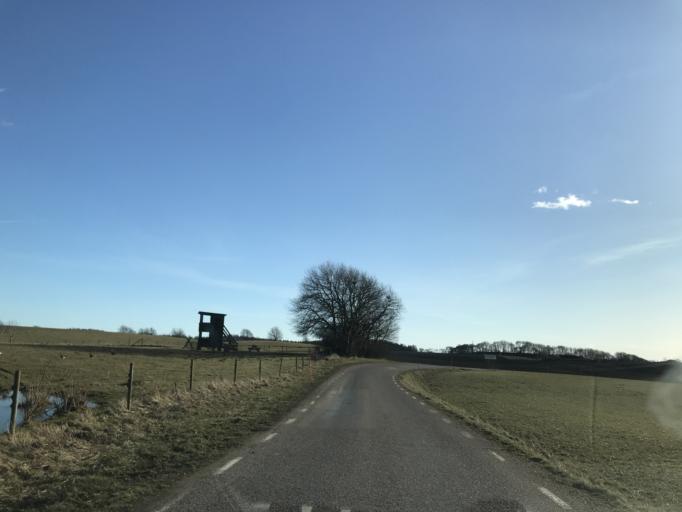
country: SE
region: Skane
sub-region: Ystads Kommun
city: Ystad
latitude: 55.5349
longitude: 13.7843
